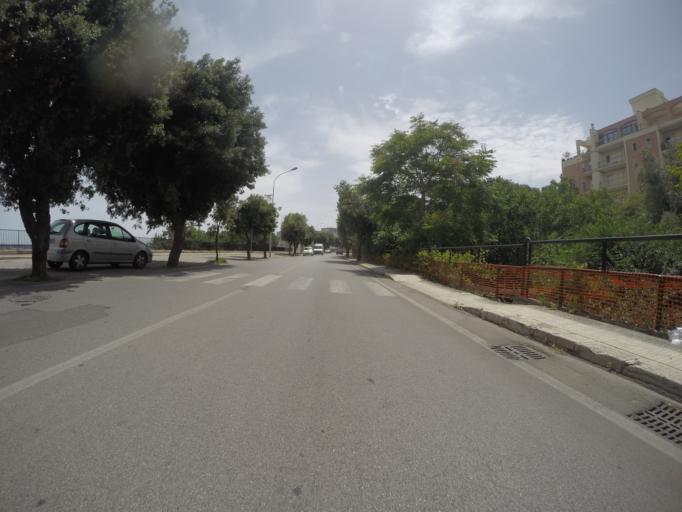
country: IT
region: Apulia
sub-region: Provincia di Taranto
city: Martina Franca
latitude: 40.7040
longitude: 17.3474
